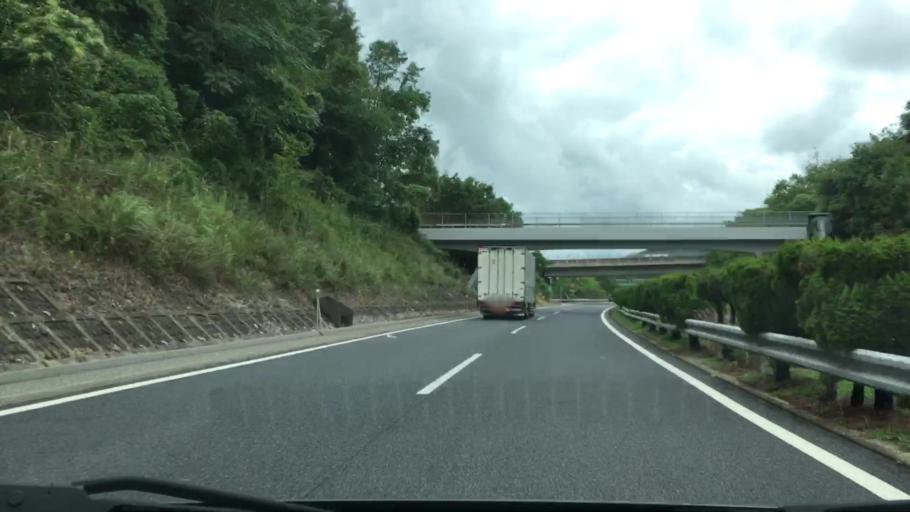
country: JP
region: Okayama
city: Tsuyama
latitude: 35.0365
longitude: 134.1332
